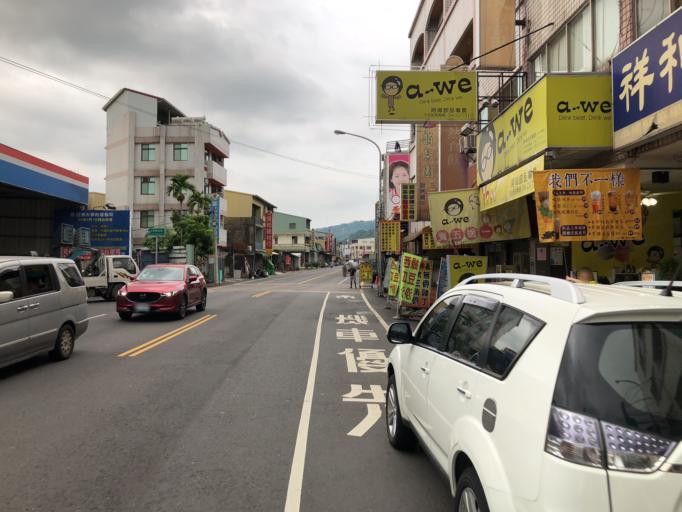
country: TW
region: Taiwan
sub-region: Taichung City
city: Taichung
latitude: 24.1120
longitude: 120.7309
